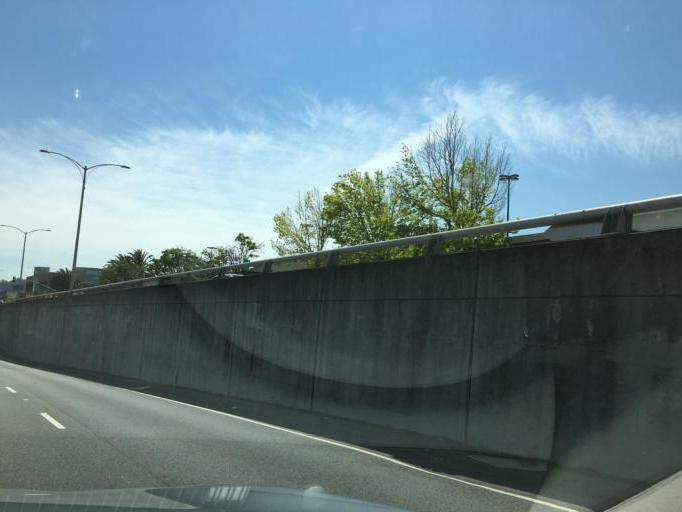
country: US
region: California
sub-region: San Mateo County
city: Belmont
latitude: 37.5380
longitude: -122.2988
